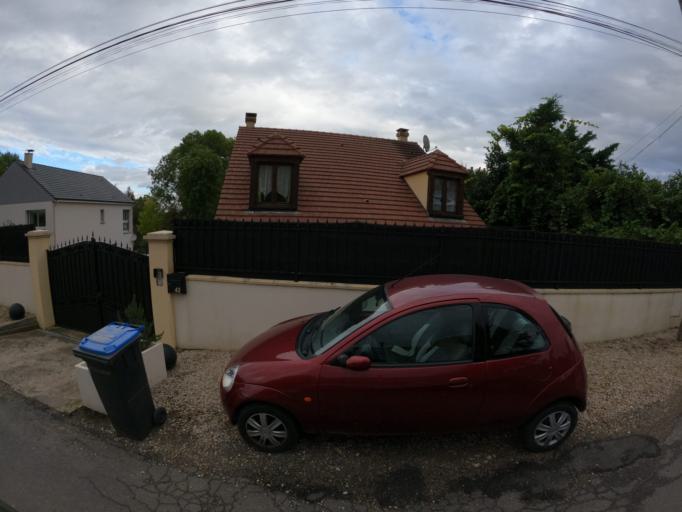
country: FR
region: Ile-de-France
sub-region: Departement de Seine-et-Marne
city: Saint-Germain-sur-Morin
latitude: 48.8730
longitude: 2.8444
